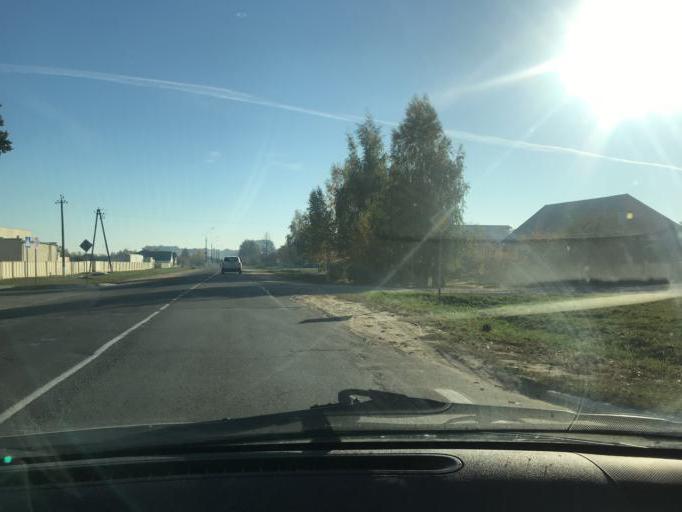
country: BY
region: Brest
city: Ivanava
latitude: 52.1433
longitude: 25.5166
